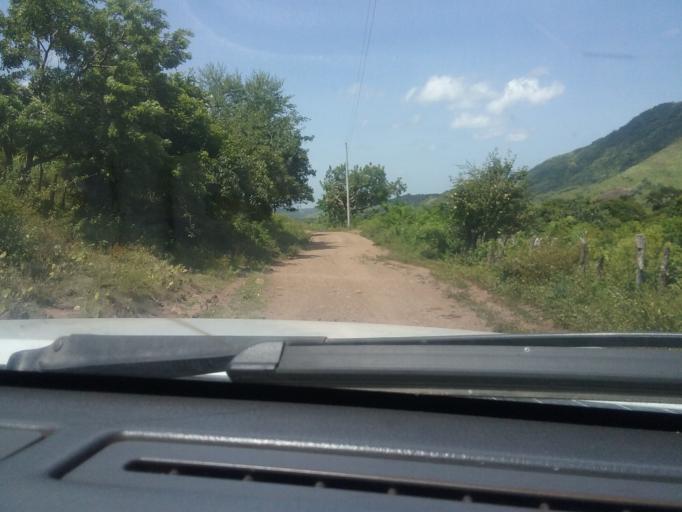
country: NI
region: Matagalpa
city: Terrabona
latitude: 12.6742
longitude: -85.9791
